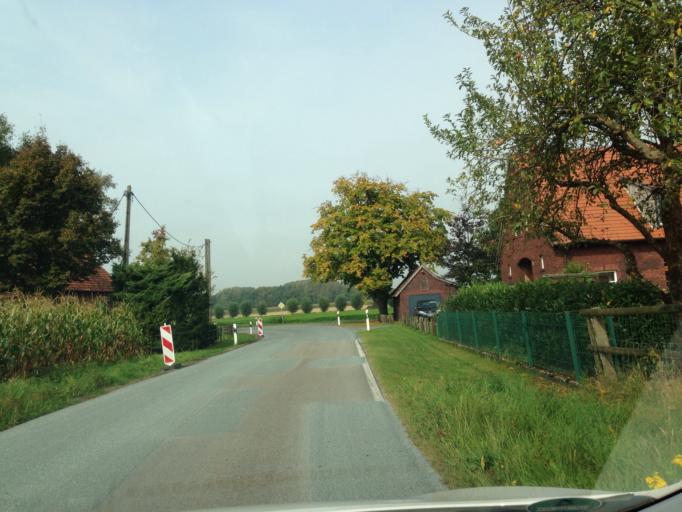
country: DE
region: North Rhine-Westphalia
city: Ludinghausen
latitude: 51.8112
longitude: 7.3941
